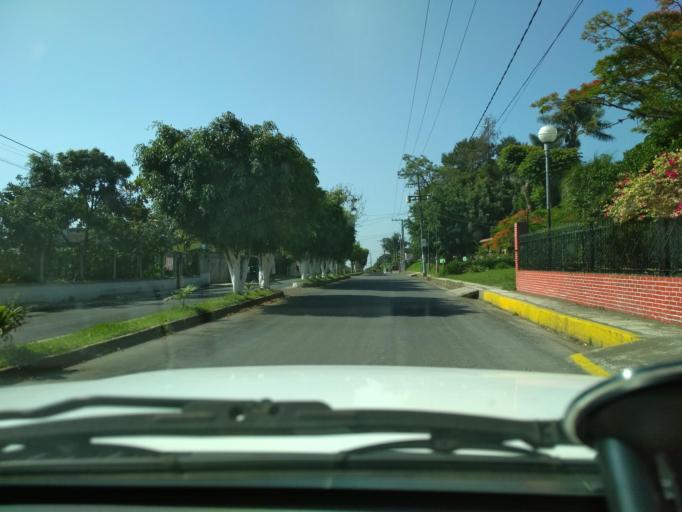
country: MX
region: Veracruz
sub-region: Chocaman
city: San Jose Neria
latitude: 18.9990
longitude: -97.0029
